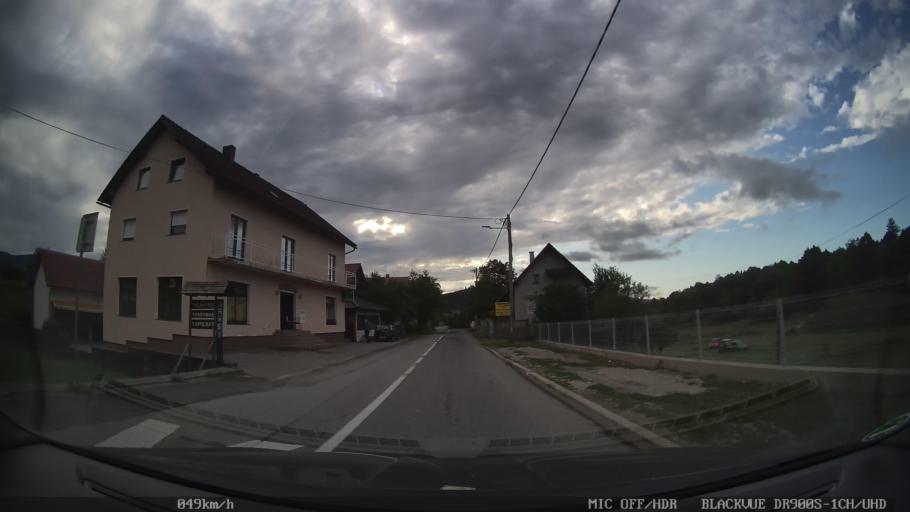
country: HR
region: Karlovacka
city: Plaski
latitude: 44.9838
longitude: 15.4776
